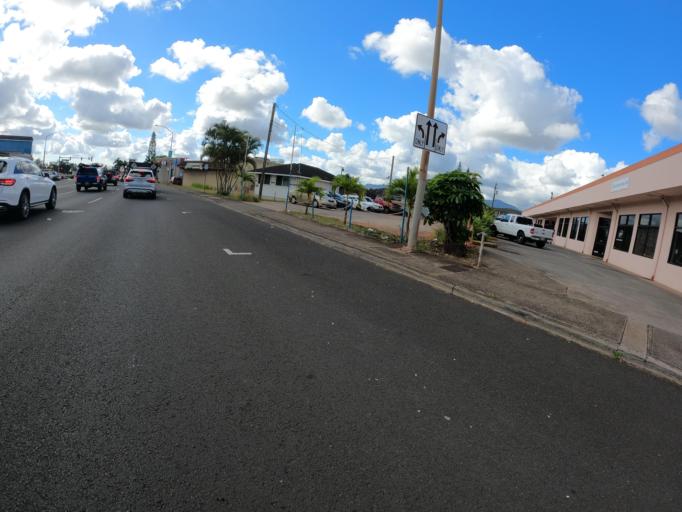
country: US
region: Hawaii
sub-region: Honolulu County
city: Wahiawa
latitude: 21.4971
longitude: -158.0300
